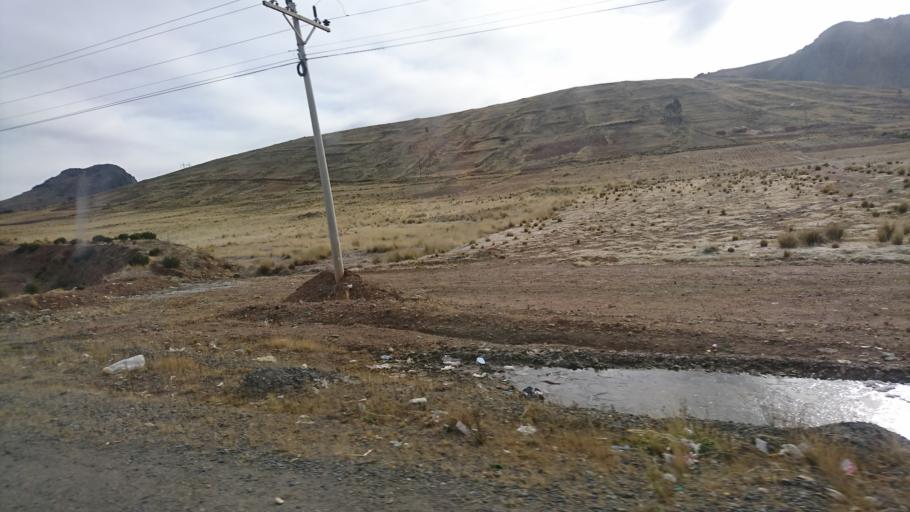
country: BO
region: La Paz
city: Batallas
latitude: -16.4113
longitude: -68.3484
